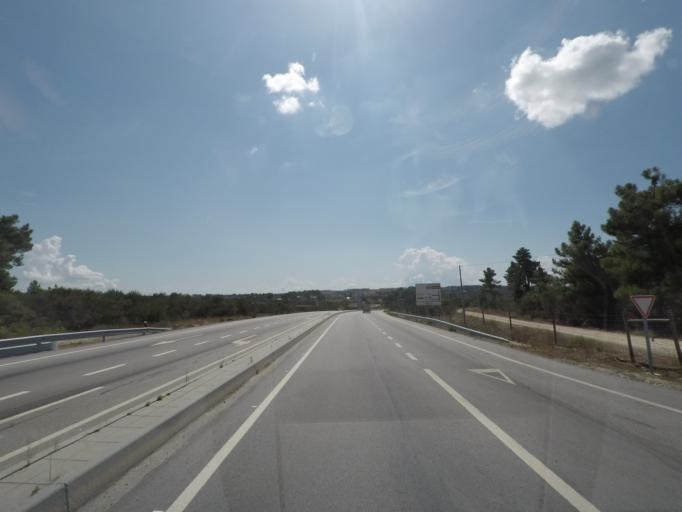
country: PT
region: Vila Real
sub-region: Murca
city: Murca
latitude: 41.3376
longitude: -7.4699
